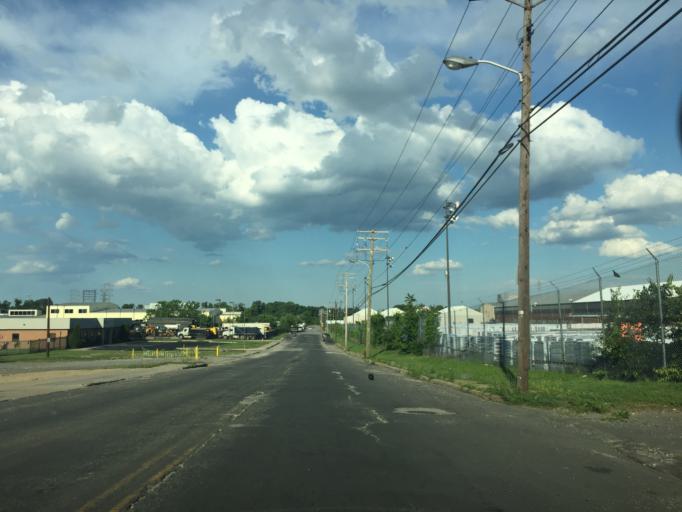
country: US
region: Maryland
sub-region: City of Baltimore
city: Baltimore
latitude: 39.3052
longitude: -76.5703
